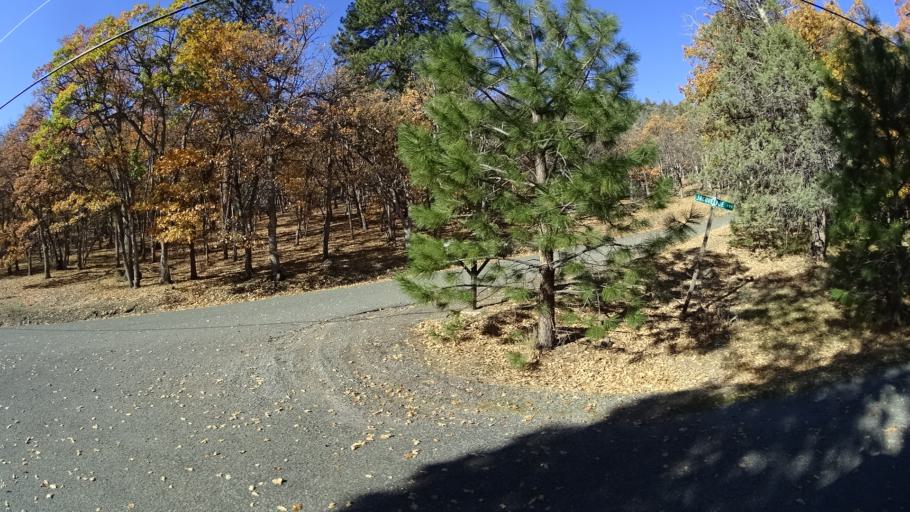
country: US
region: California
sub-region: Siskiyou County
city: Montague
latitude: 41.9714
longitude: -122.3032
